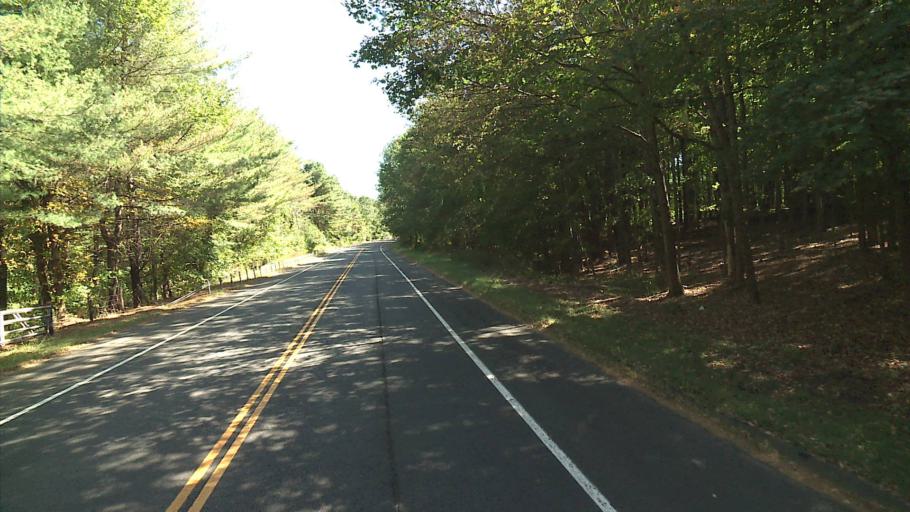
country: US
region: Connecticut
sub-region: New Haven County
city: Cheshire Village
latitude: 41.4976
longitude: -72.8604
